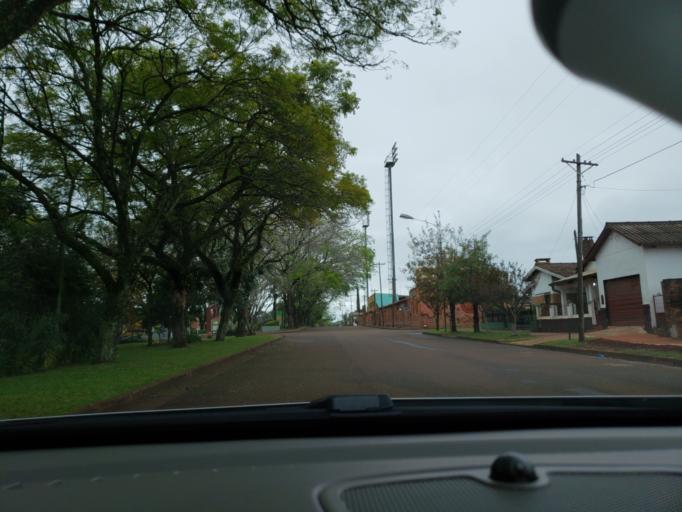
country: AR
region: Misiones
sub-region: Departamento de Apostoles
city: Apostoles
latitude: -27.9097
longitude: -55.7501
